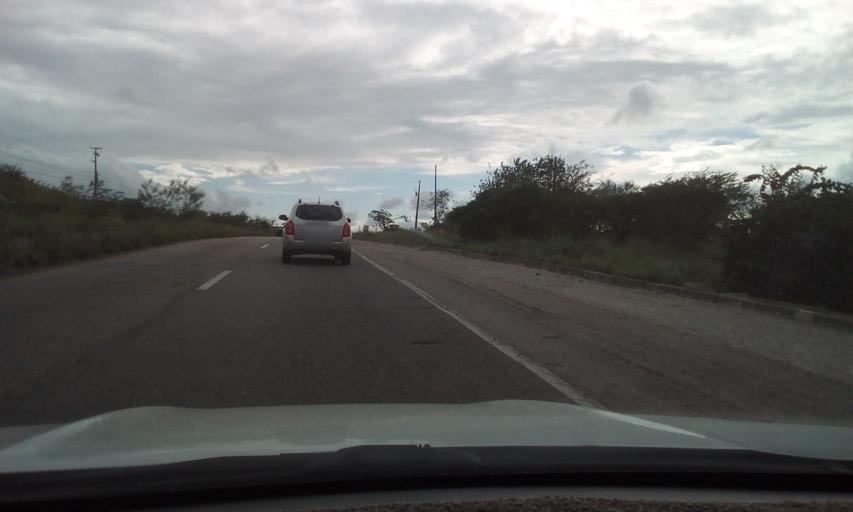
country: BR
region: Pernambuco
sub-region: Gravata
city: Gravata
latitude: -8.1953
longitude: -35.5183
